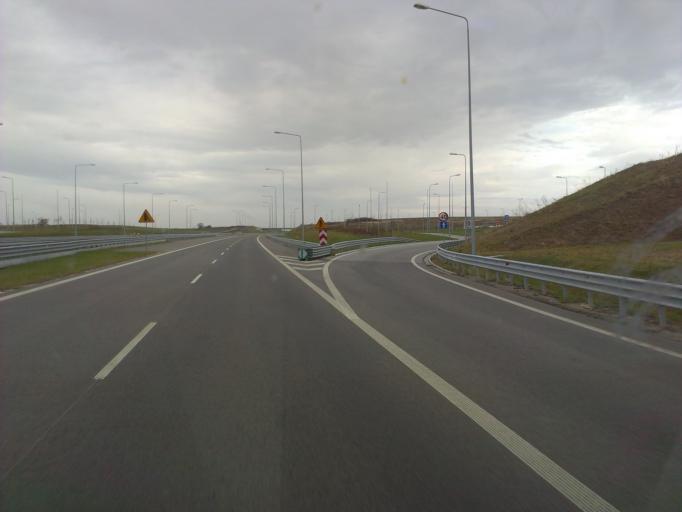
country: PL
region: Subcarpathian Voivodeship
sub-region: Powiat jaroslawski
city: Pawlosiow
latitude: 49.9932
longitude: 22.6085
